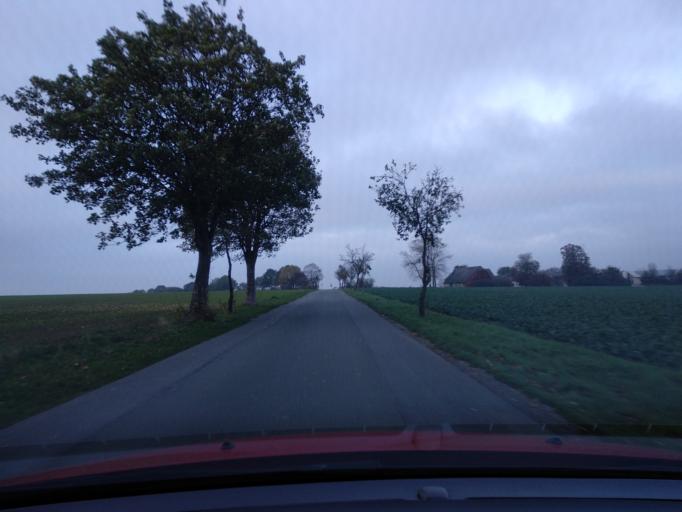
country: DE
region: North Rhine-Westphalia
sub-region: Regierungsbezirk Detmold
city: Paderborn
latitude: 51.6774
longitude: 8.7697
